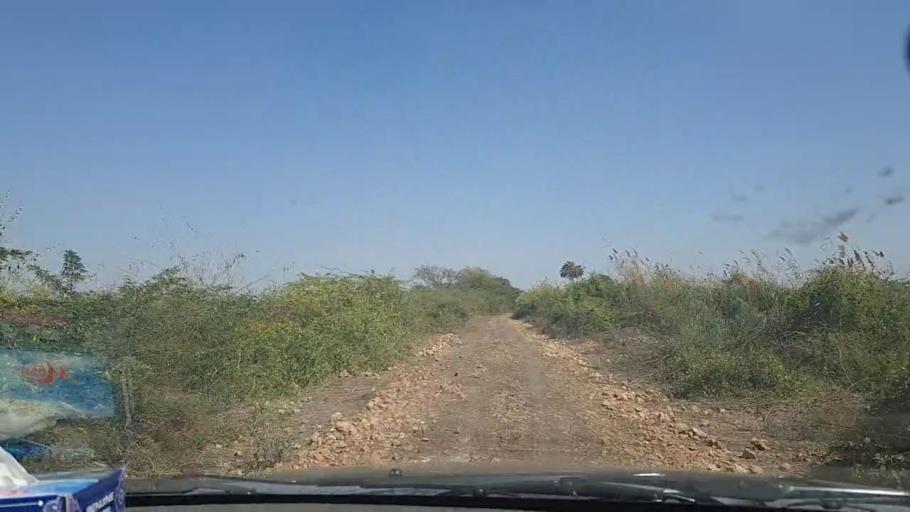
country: PK
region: Sindh
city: Chuhar Jamali
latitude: 24.2736
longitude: 67.7406
